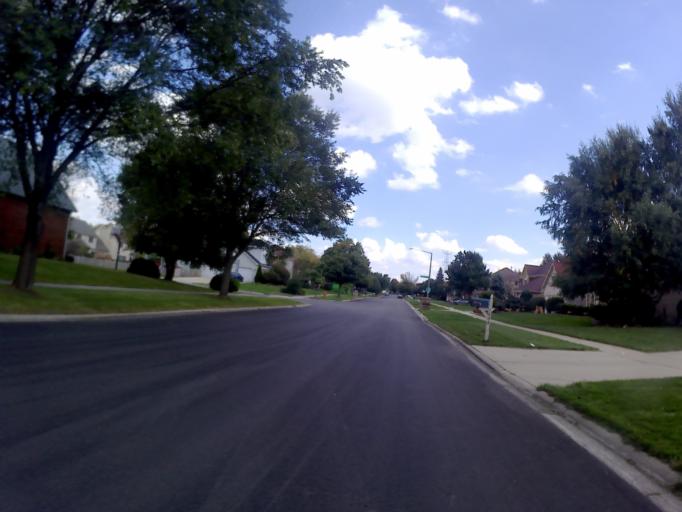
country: US
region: Illinois
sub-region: DuPage County
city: Woodridge
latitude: 41.7389
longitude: -88.0929
